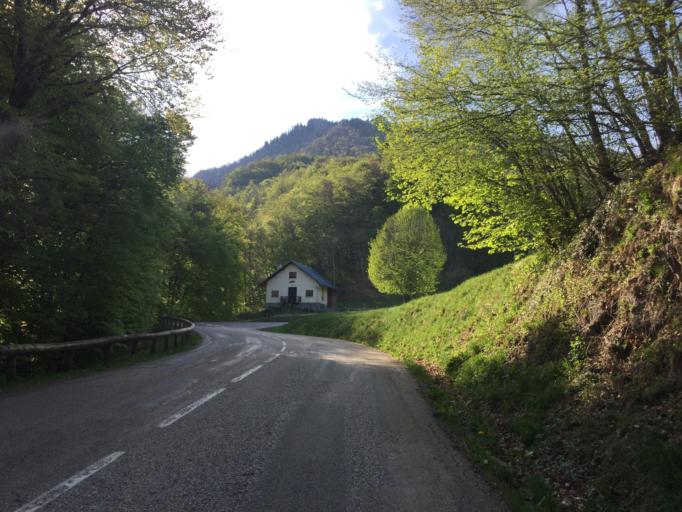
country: FR
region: Rhone-Alpes
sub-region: Departement de la Savoie
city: Mercury
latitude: 45.6687
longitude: 6.3070
